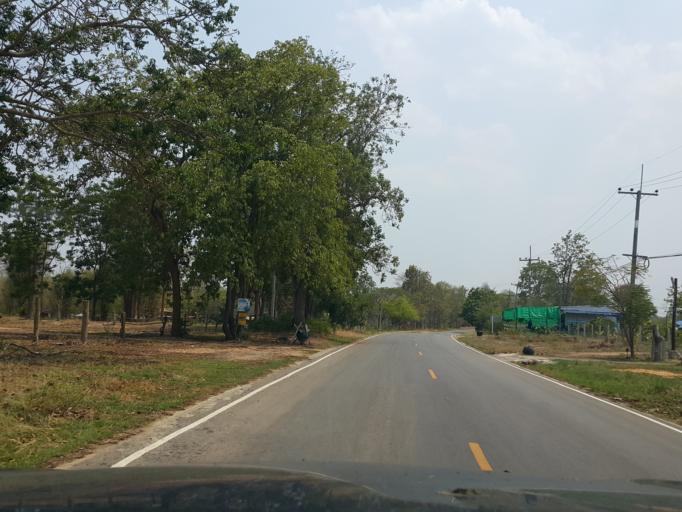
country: TH
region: Lampang
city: Mae Phrik
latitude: 17.4911
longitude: 99.1246
